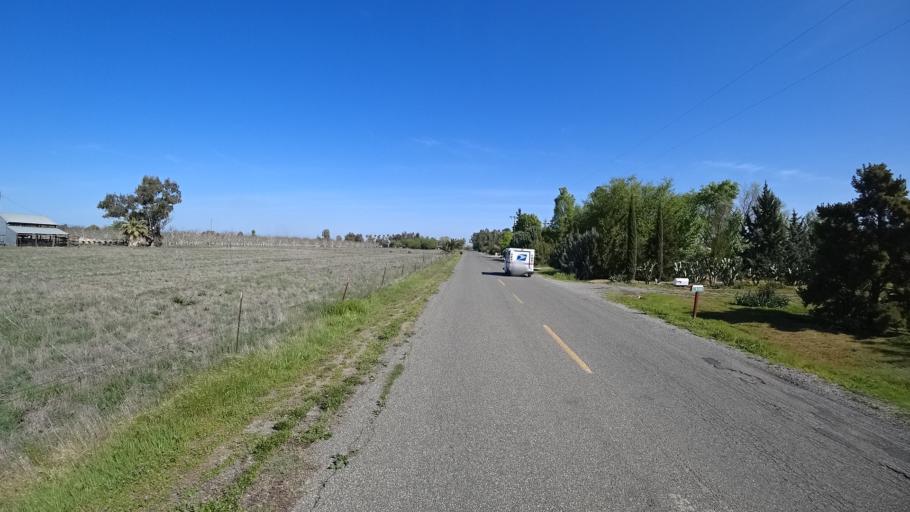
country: US
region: California
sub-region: Glenn County
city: Willows
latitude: 39.5334
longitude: -122.1887
